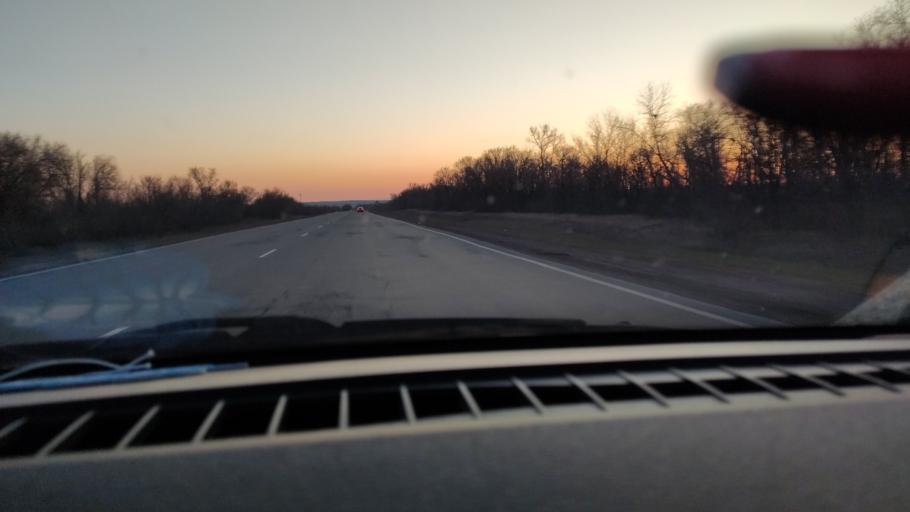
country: RU
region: Saratov
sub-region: Saratovskiy Rayon
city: Saratov
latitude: 51.7116
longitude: 46.0202
